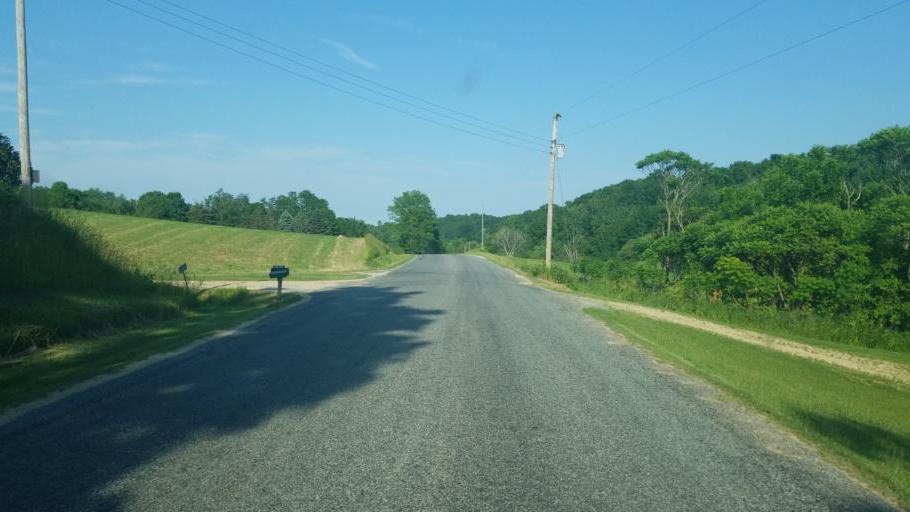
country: US
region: Wisconsin
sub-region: Vernon County
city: Hillsboro
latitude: 43.6813
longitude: -90.3627
